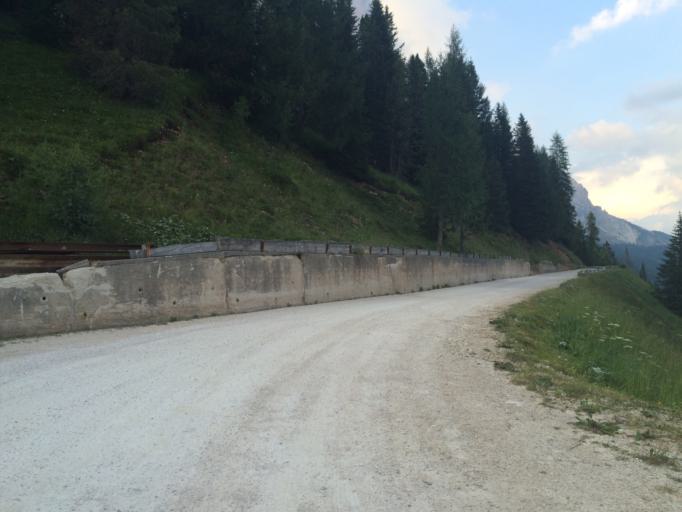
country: IT
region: Veneto
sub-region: Provincia di Belluno
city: Selva di Cadore
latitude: 46.5192
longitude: 12.0367
